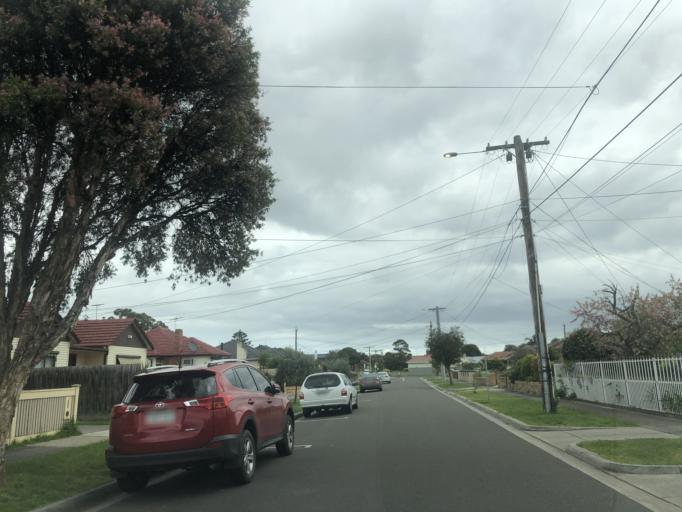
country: AU
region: Victoria
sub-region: Greater Dandenong
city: Dandenong North
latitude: -37.9756
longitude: 145.2145
